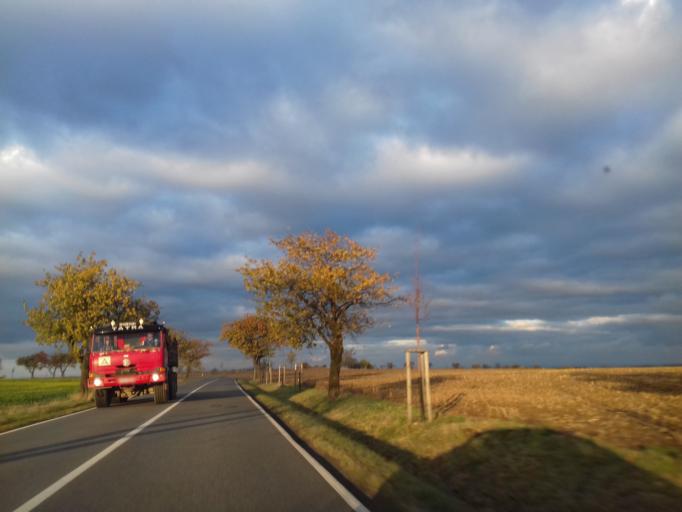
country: CZ
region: Pardubicky
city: Krouna
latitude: 49.8056
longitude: 16.0426
